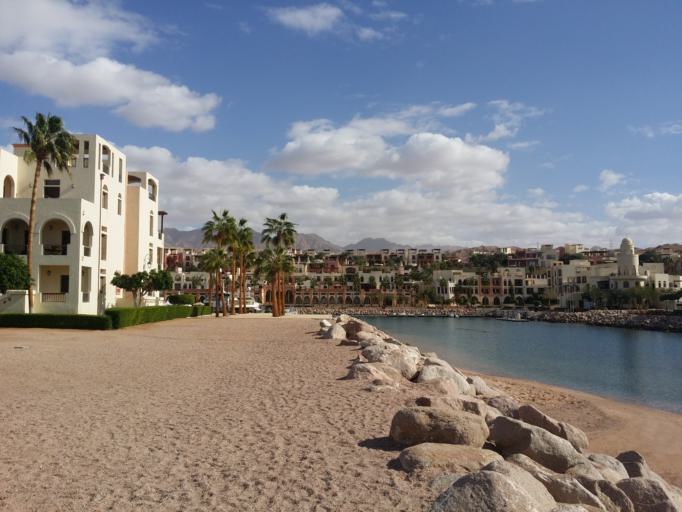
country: JO
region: Aqaba
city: Aqaba
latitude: 29.4092
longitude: 34.9777
